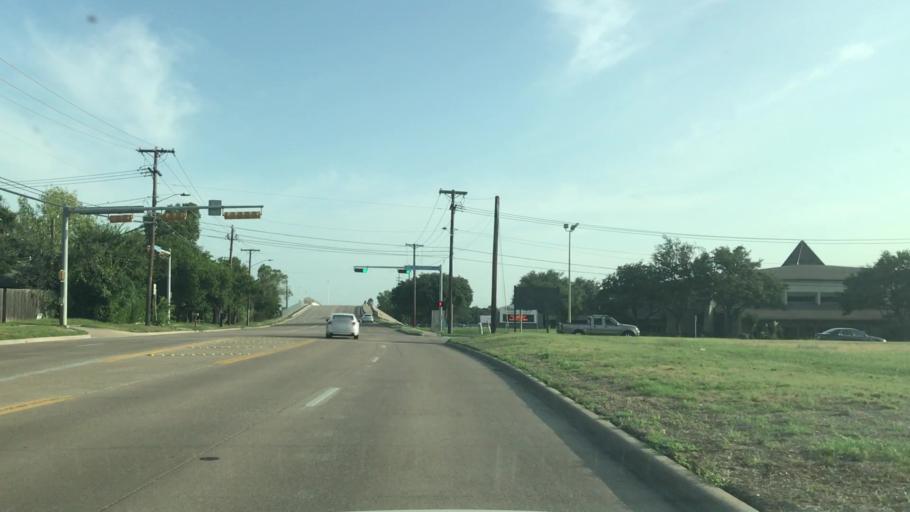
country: US
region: Texas
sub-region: Tarrant County
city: Arlington
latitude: 32.7570
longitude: -97.1231
